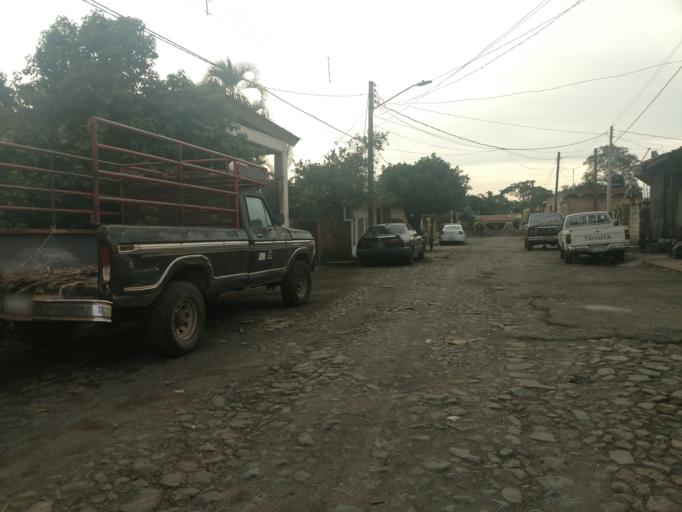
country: MX
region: Nayarit
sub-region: Tepic
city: La Corregidora
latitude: 21.4634
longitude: -104.8033
